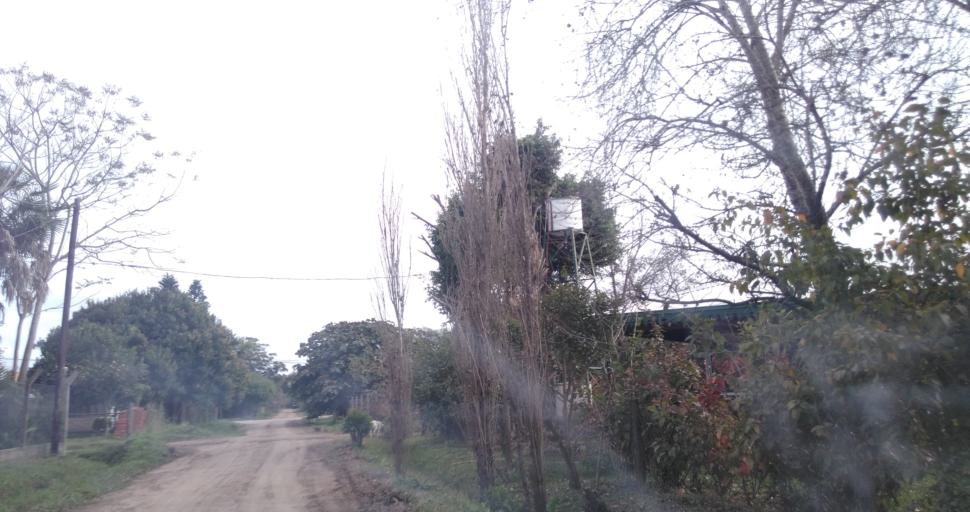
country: AR
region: Chaco
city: Colonia Benitez
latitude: -27.3283
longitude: -58.9532
